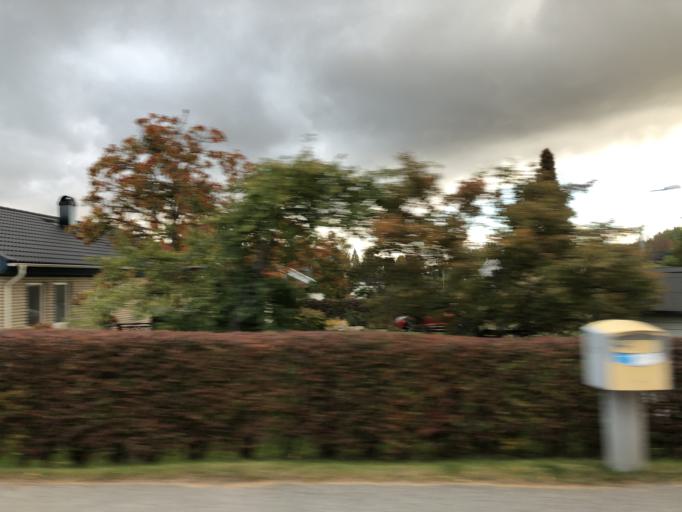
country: SE
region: Stockholm
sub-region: Jarfalla Kommun
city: Jakobsberg
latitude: 59.4230
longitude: 17.8074
